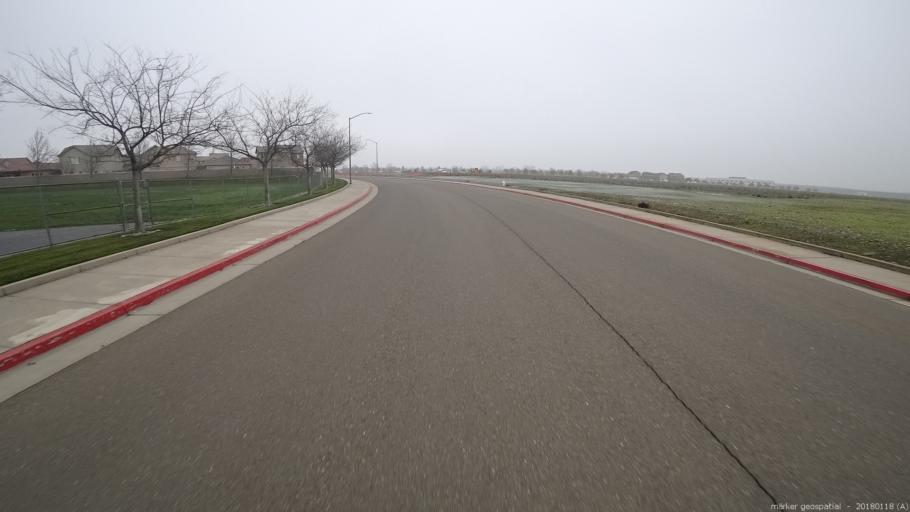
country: US
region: California
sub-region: Sacramento County
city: Rancho Cordova
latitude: 38.5726
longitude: -121.2837
